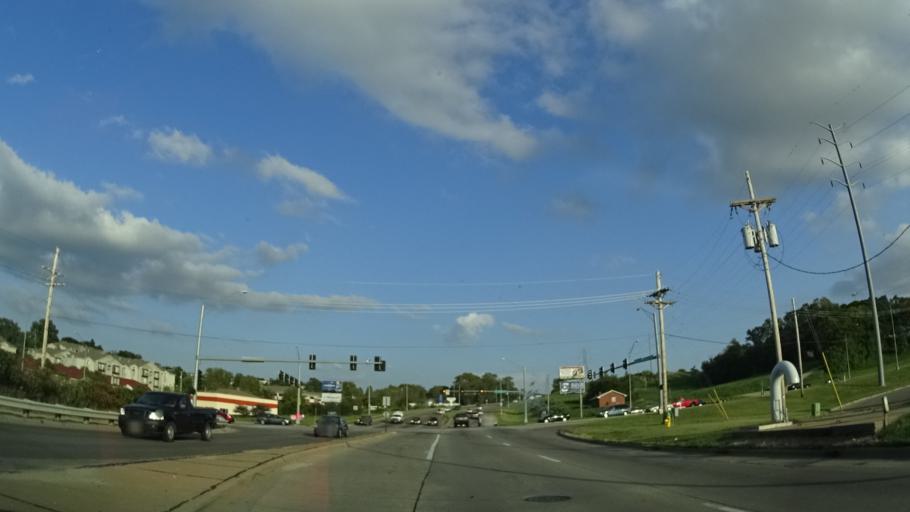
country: US
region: Nebraska
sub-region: Sarpy County
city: Offutt Air Force Base
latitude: 41.1568
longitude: -95.9271
